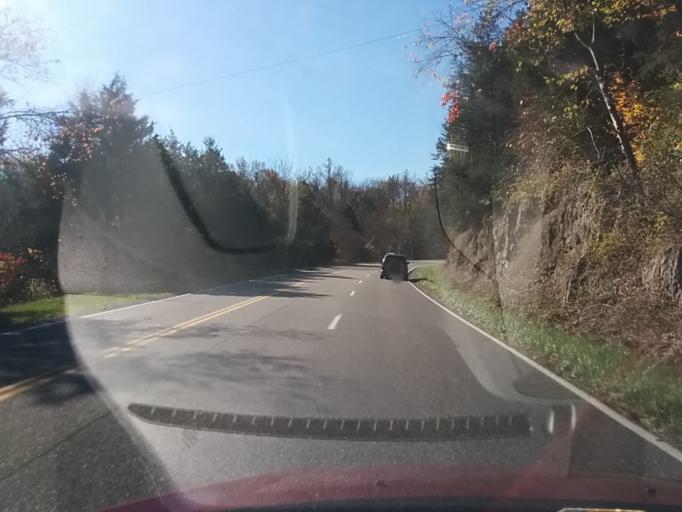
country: US
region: Virginia
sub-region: City of Lexington
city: Lexington
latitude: 37.7557
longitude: -79.4519
